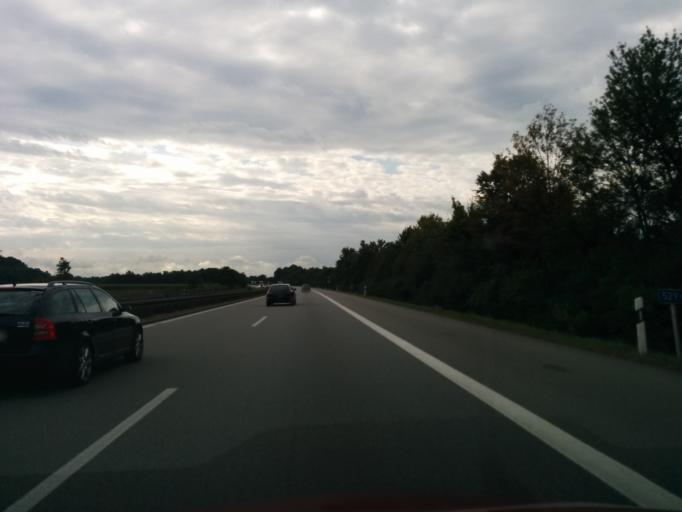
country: DE
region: Bavaria
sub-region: Lower Bavaria
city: Kirchroth
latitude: 48.9519
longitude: 12.5572
